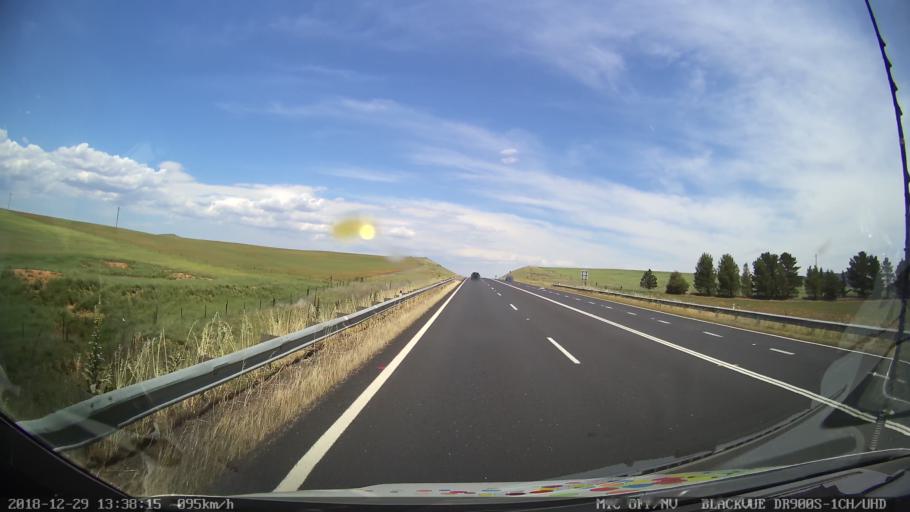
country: AU
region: New South Wales
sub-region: Cooma-Monaro
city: Cooma
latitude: -35.9958
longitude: 149.1406
